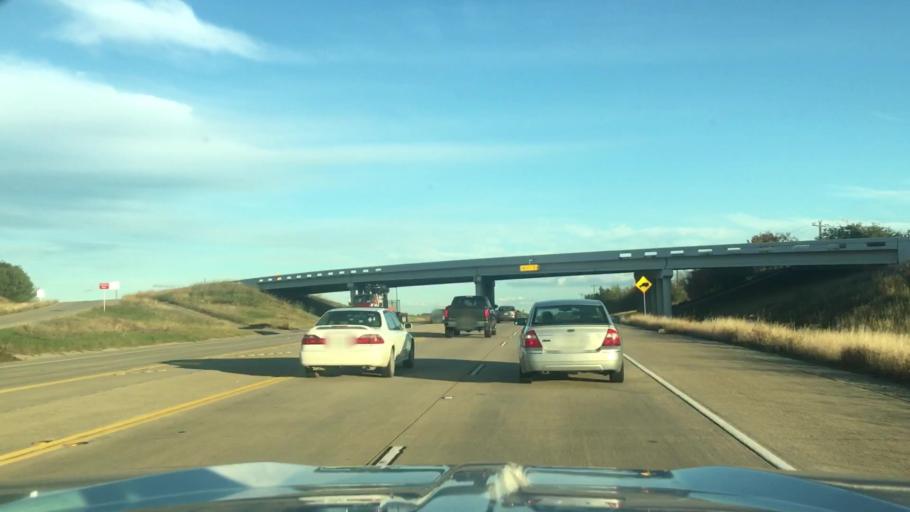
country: US
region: Texas
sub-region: Denton County
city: Cross Roads
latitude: 33.2319
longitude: -97.0061
